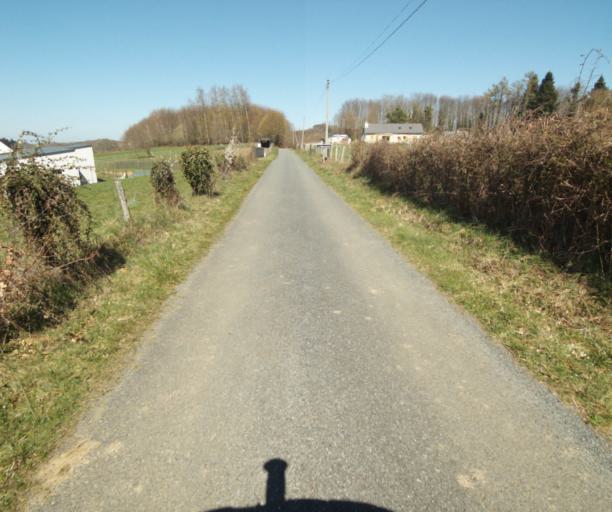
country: FR
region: Limousin
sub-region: Departement de la Correze
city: Saint-Clement
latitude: 45.3345
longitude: 1.6942
